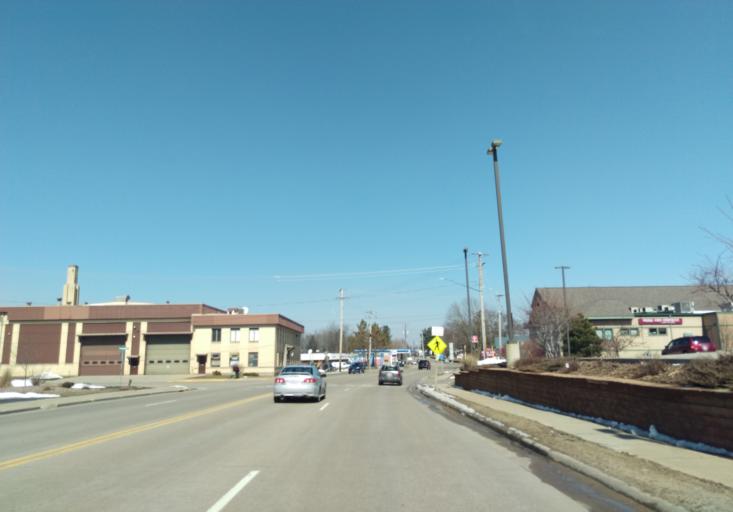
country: US
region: Wisconsin
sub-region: Vernon County
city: Viroqua
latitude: 43.5598
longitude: -90.8893
